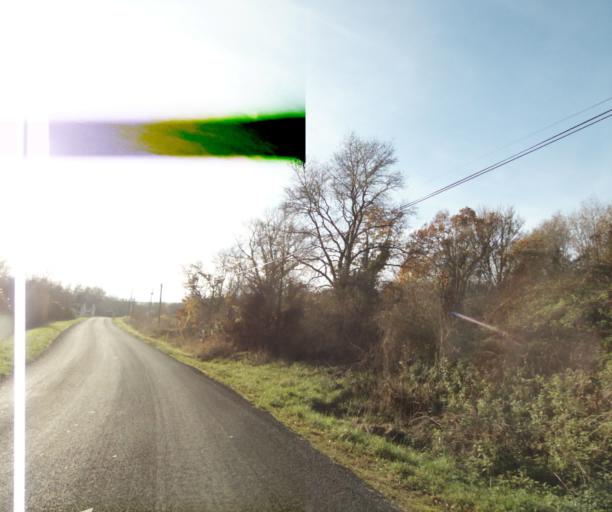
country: FR
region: Poitou-Charentes
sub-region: Departement de la Charente-Maritime
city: Chaniers
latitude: 45.7268
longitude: -0.5171
